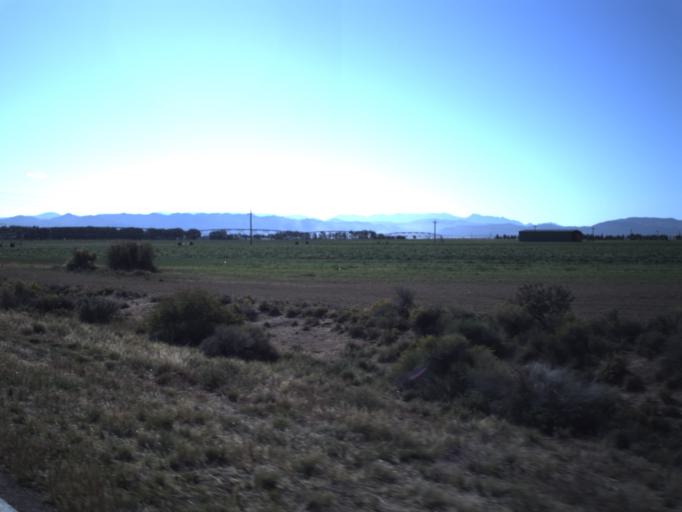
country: US
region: Utah
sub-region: Washington County
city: Enterprise
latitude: 37.7265
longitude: -113.7037
